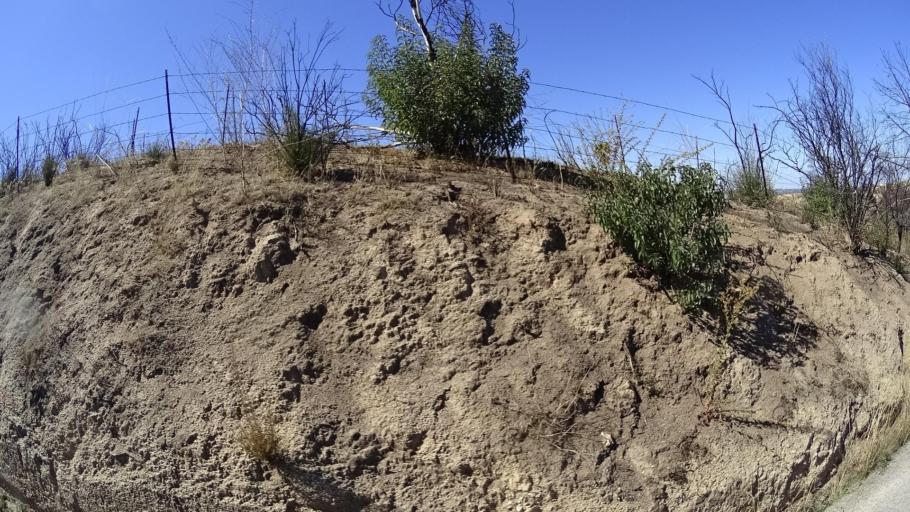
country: US
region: California
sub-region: San Diego County
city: Alpine
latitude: 32.7716
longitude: -116.7631
